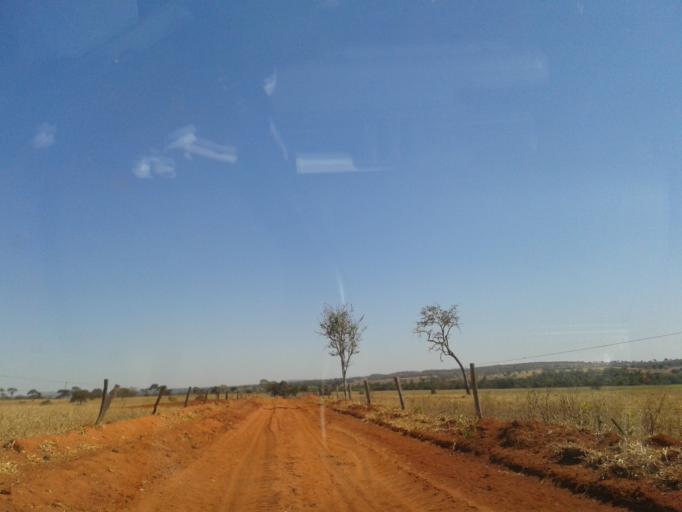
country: BR
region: Minas Gerais
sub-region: Santa Vitoria
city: Santa Vitoria
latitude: -19.0783
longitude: -50.0656
